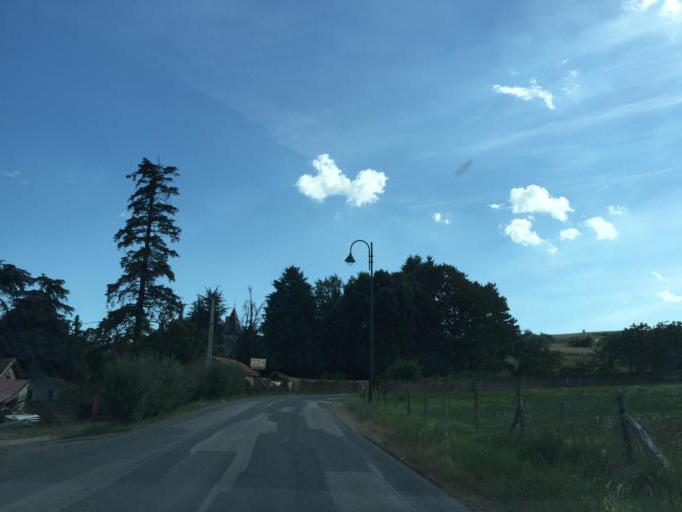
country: FR
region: Rhone-Alpes
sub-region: Departement de la Loire
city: Saint-Julien-Molin-Molette
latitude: 45.3238
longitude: 4.6106
